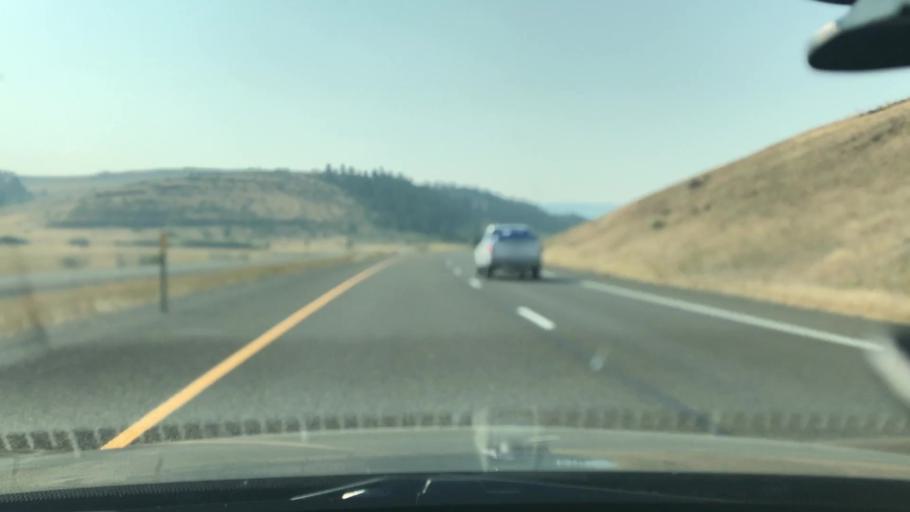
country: US
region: Oregon
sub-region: Union County
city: Union
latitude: 45.1739
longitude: -117.9762
